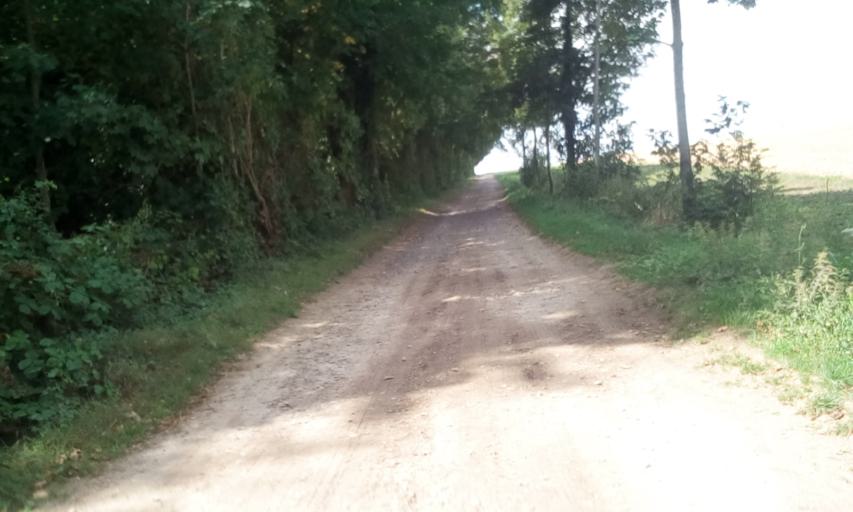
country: FR
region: Lower Normandy
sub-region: Departement du Calvados
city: Bourguebus
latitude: 49.1036
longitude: -0.2635
